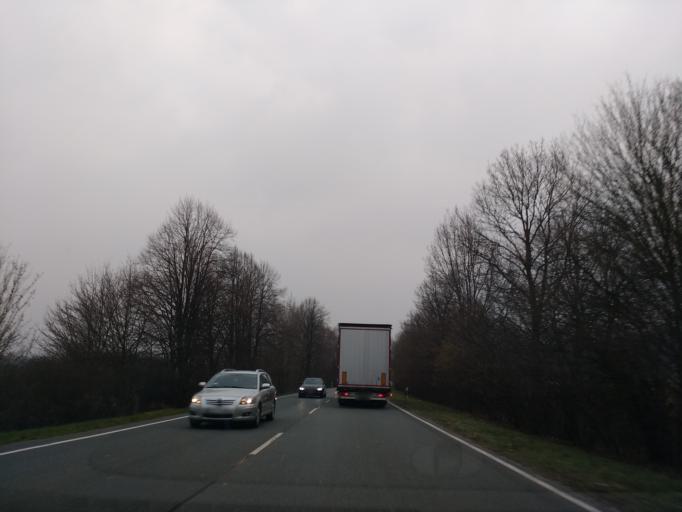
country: DE
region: North Rhine-Westphalia
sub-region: Regierungsbezirk Munster
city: Lotte
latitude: 52.2712
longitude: 7.8946
